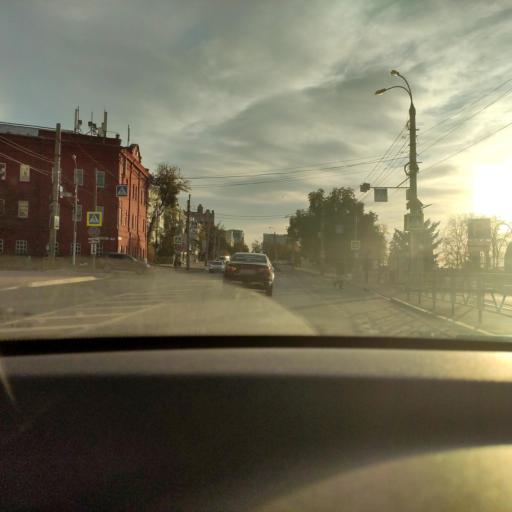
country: RU
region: Samara
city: Rozhdestveno
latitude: 53.1919
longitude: 50.0862
